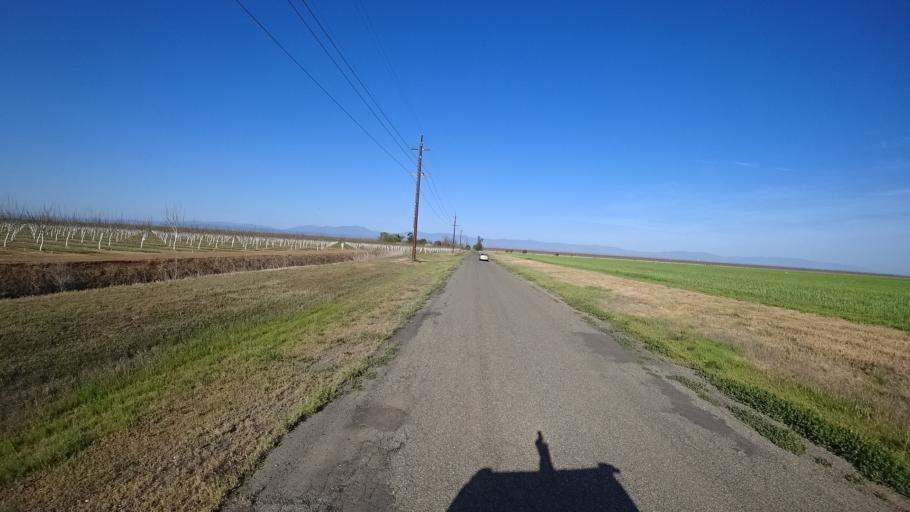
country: US
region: California
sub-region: Glenn County
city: Willows
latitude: 39.5535
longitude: -122.2254
